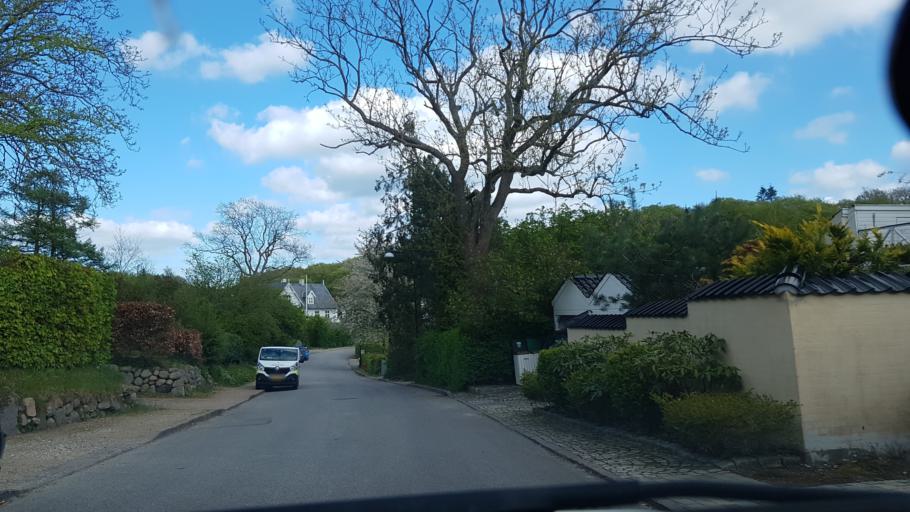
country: DK
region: Capital Region
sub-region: Rudersdal Kommune
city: Holte
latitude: 55.8170
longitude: 12.4908
